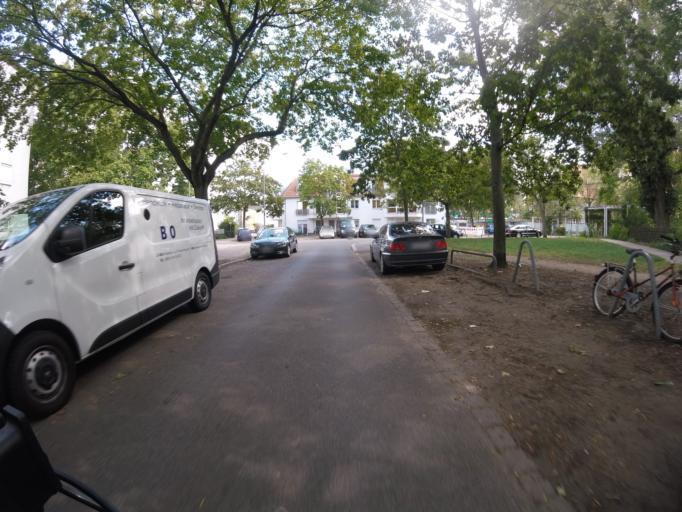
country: DE
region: Berlin
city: Spandau
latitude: 52.5495
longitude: 13.1971
